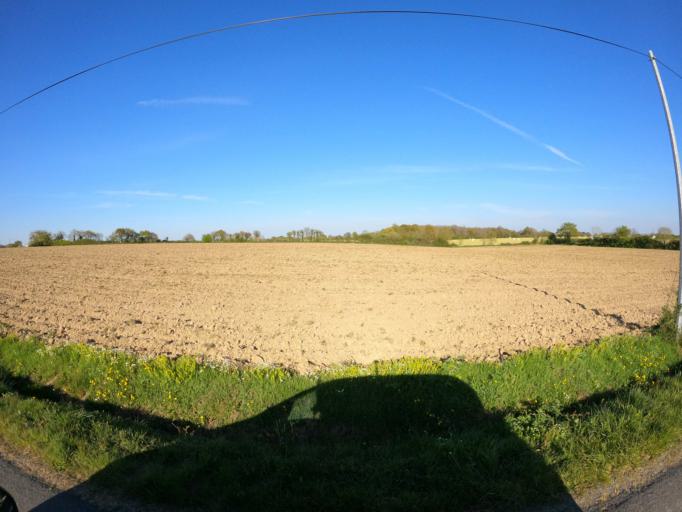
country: FR
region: Pays de la Loire
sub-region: Departement de la Vendee
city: Les Brouzils
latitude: 46.8941
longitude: -1.3680
